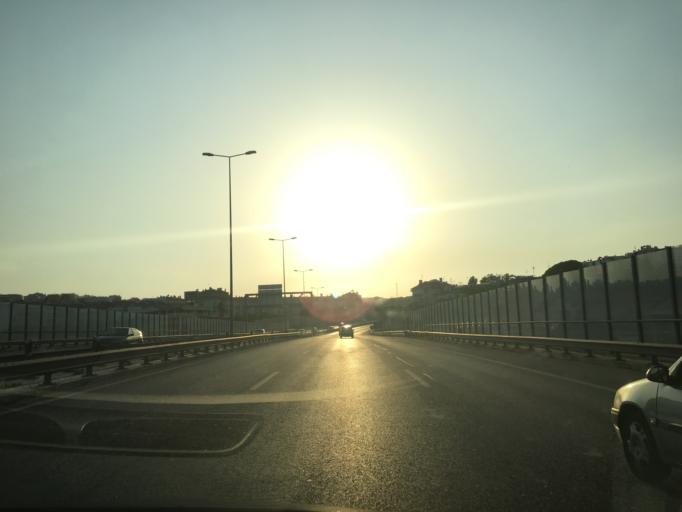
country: PT
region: Lisbon
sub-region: Oeiras
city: Barcarena
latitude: 38.7489
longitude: -9.2820
